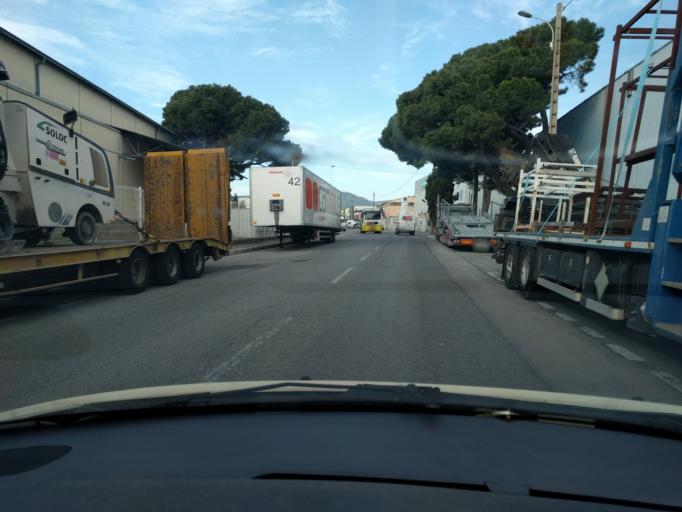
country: FR
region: Provence-Alpes-Cote d'Azur
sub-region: Departement des Alpes-Maritimes
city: Mandelieu-la-Napoule
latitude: 43.5447
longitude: 6.9634
